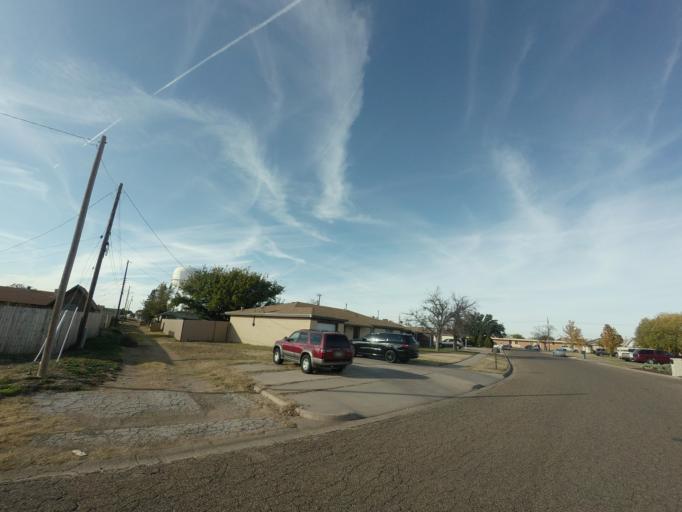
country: US
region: New Mexico
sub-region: Curry County
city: Clovis
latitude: 34.4254
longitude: -103.2255
